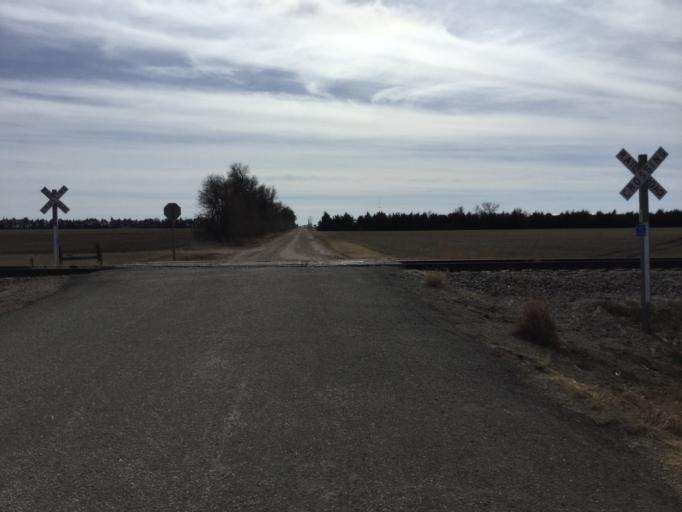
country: US
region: Kansas
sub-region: Rice County
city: Lyons
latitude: 38.5147
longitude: -98.3311
